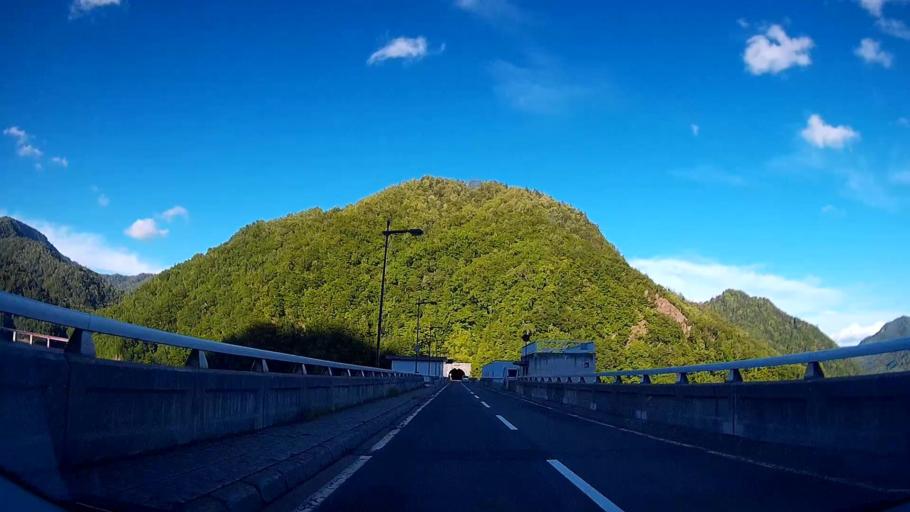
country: JP
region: Hokkaido
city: Sapporo
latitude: 42.9849
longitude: 141.1564
